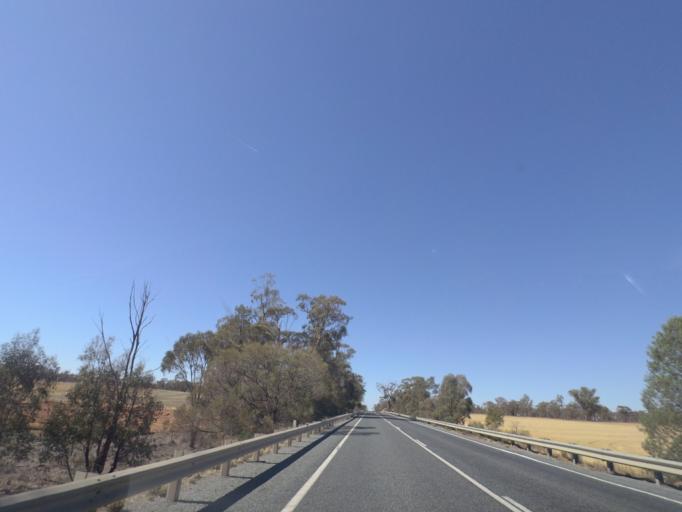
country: AU
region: New South Wales
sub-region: Bland
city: West Wyalong
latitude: -34.1643
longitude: 147.1162
